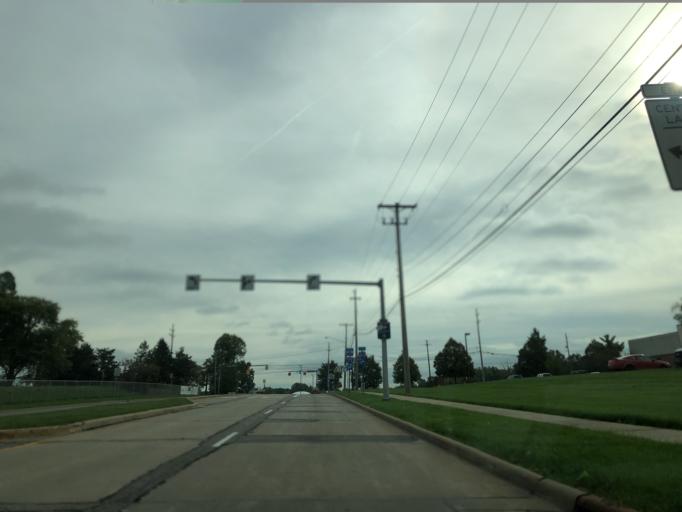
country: US
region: Ohio
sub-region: Cuyahoga County
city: Brecksville
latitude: 41.2893
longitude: -81.6292
